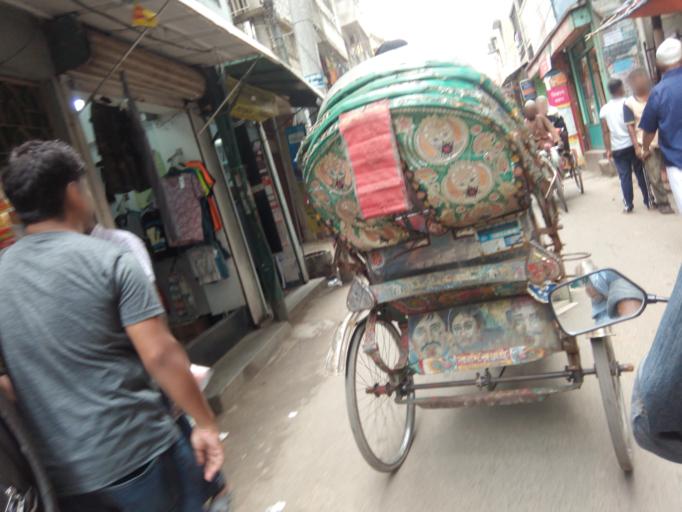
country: BD
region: Dhaka
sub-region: Dhaka
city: Dhaka
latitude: 23.7102
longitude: 90.4141
